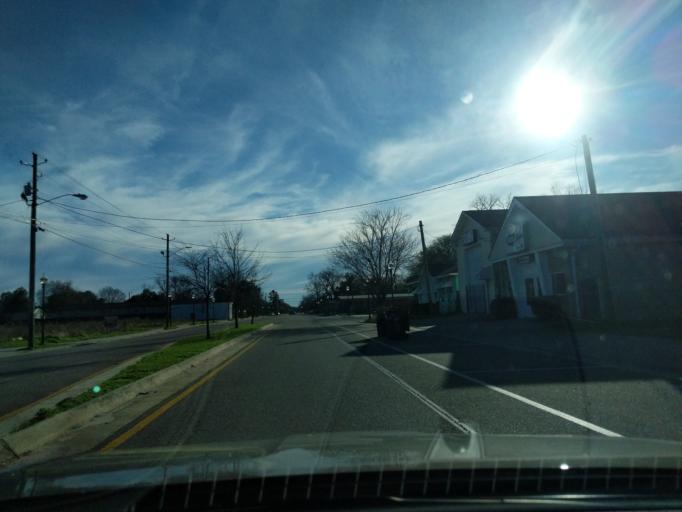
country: US
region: Georgia
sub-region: Richmond County
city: Augusta
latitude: 33.4680
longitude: -81.9486
